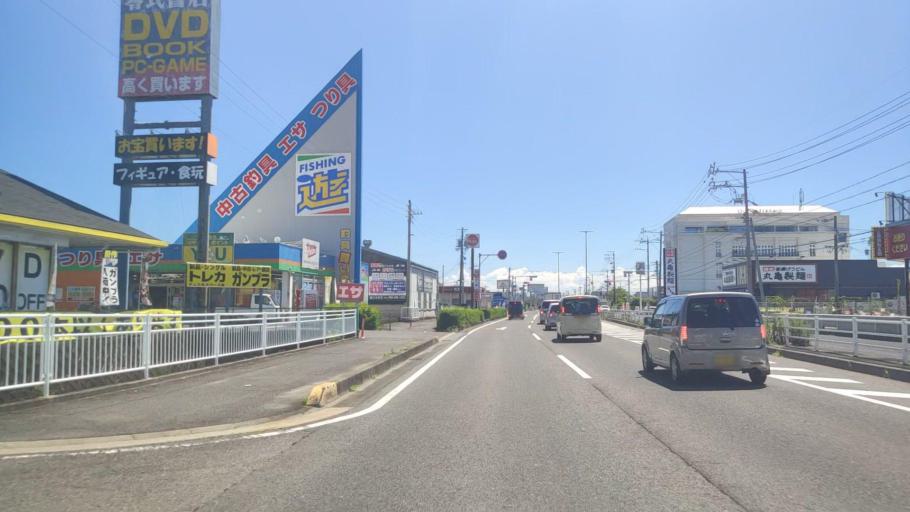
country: JP
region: Mie
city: Kawage
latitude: 34.8310
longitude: 136.5826
